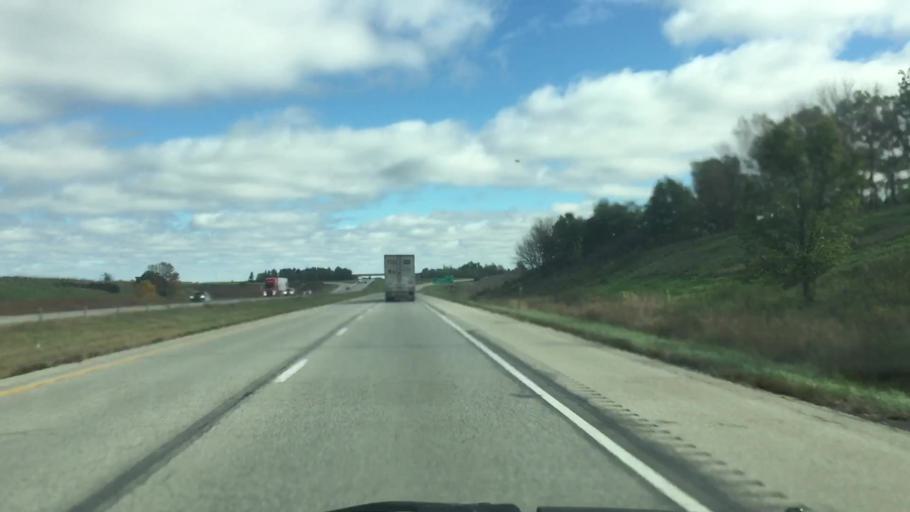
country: US
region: Iowa
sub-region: Poweshiek County
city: Grinnell
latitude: 41.6952
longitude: -92.8078
